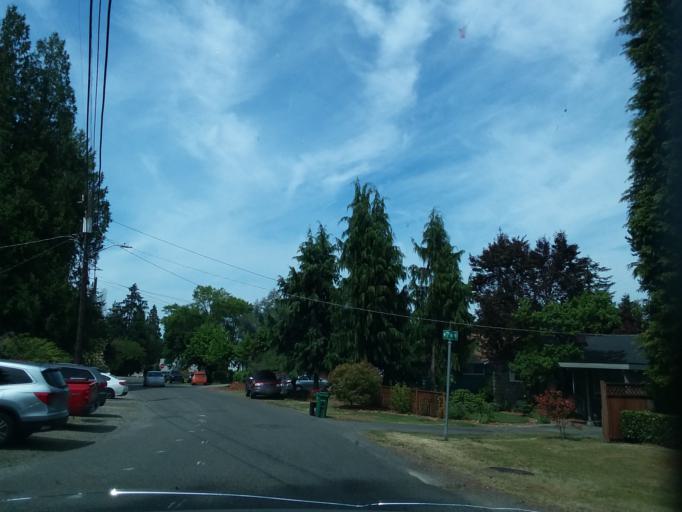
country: US
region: Washington
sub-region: King County
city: Lake Forest Park
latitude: 47.7184
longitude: -122.3100
